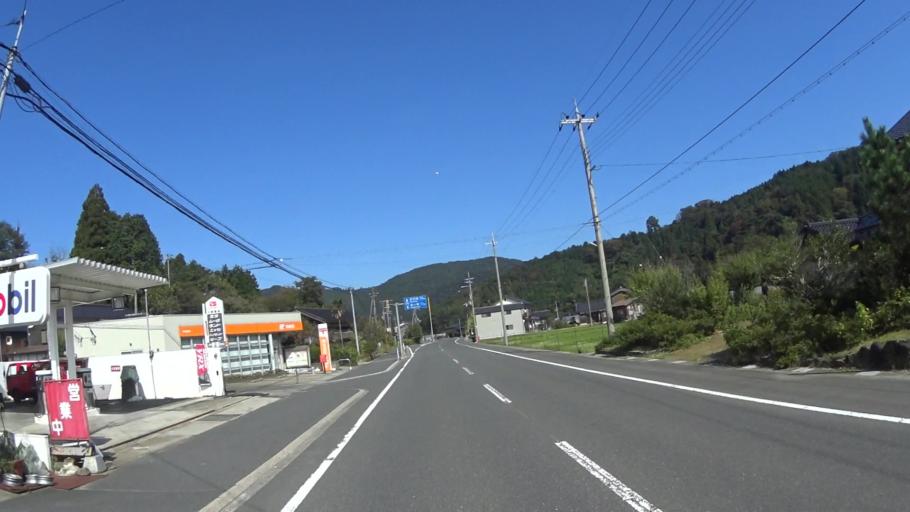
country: JP
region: Kyoto
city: Miyazu
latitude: 35.7221
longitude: 135.2535
